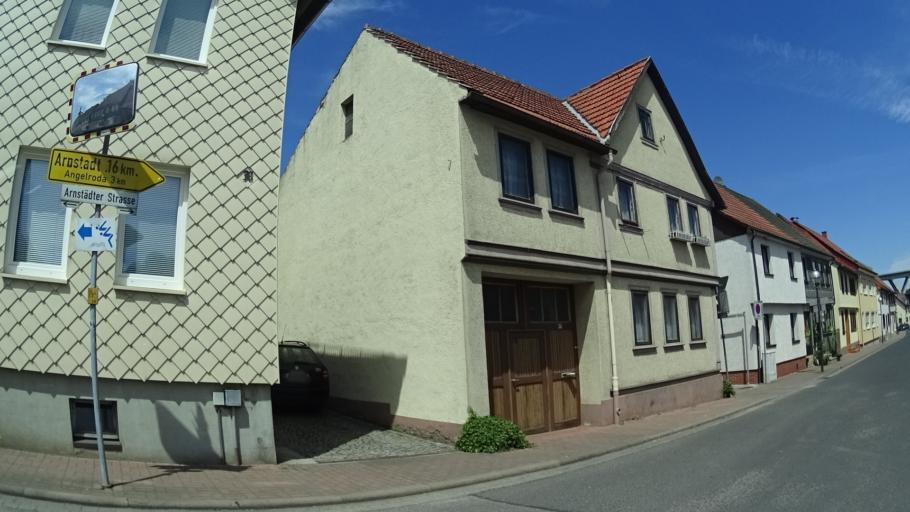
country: DE
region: Thuringia
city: Geraberg
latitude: 50.7197
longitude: 10.8481
